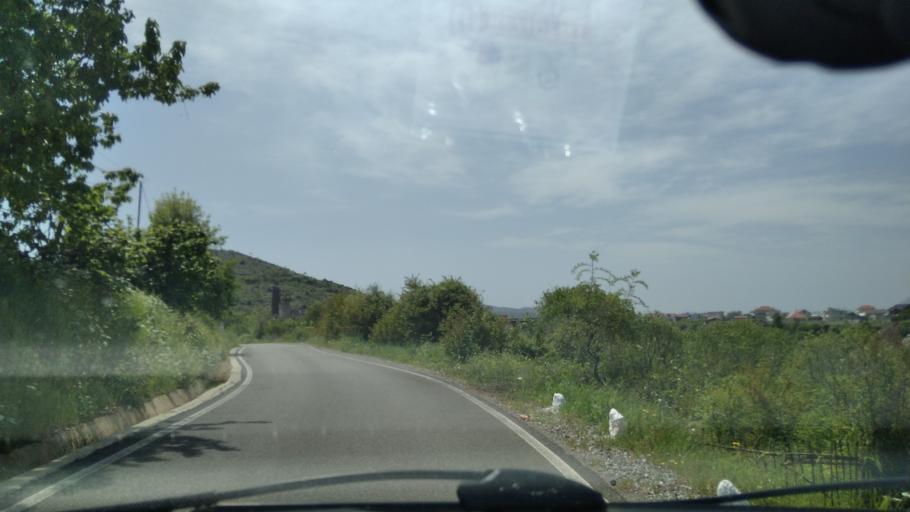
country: AL
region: Shkoder
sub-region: Rrethi i Malesia e Madhe
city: Gruemire
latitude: 42.1209
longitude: 19.5791
